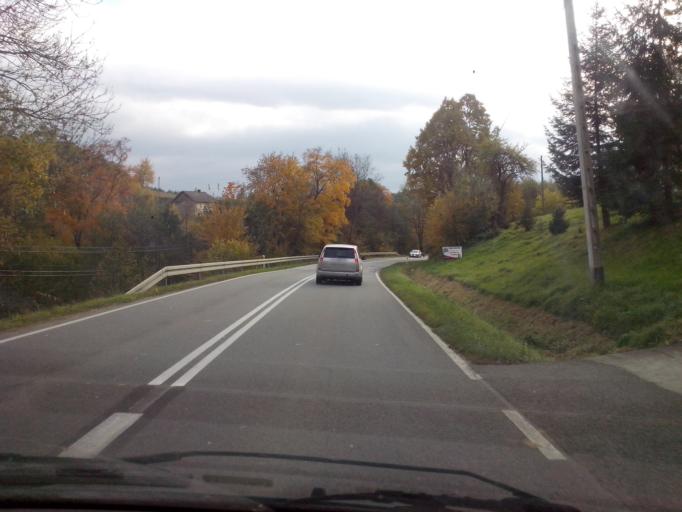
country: PL
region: Subcarpathian Voivodeship
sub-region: Powiat strzyzowski
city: Wisniowa
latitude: 49.8840
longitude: 21.6474
